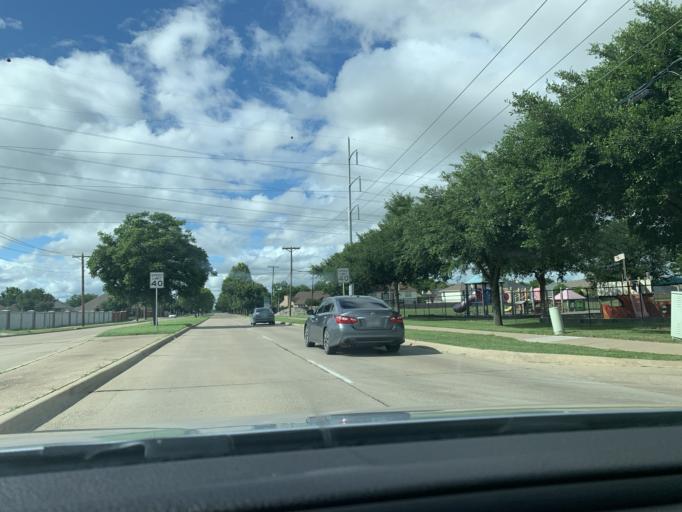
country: US
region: Texas
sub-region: Dallas County
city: Grand Prairie
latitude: 32.6590
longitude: -97.0153
